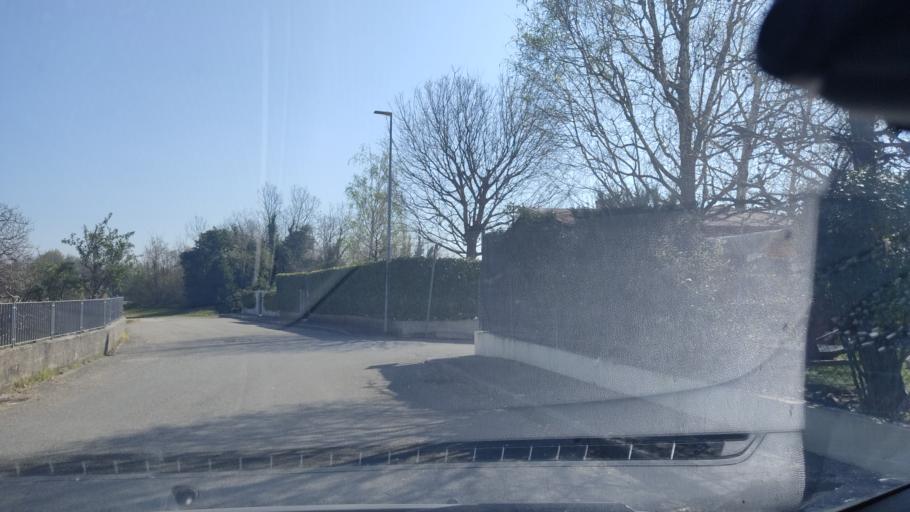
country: IT
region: Friuli Venezia Giulia
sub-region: Provincia di Pordenone
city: Budoia
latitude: 46.0485
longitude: 12.5364
